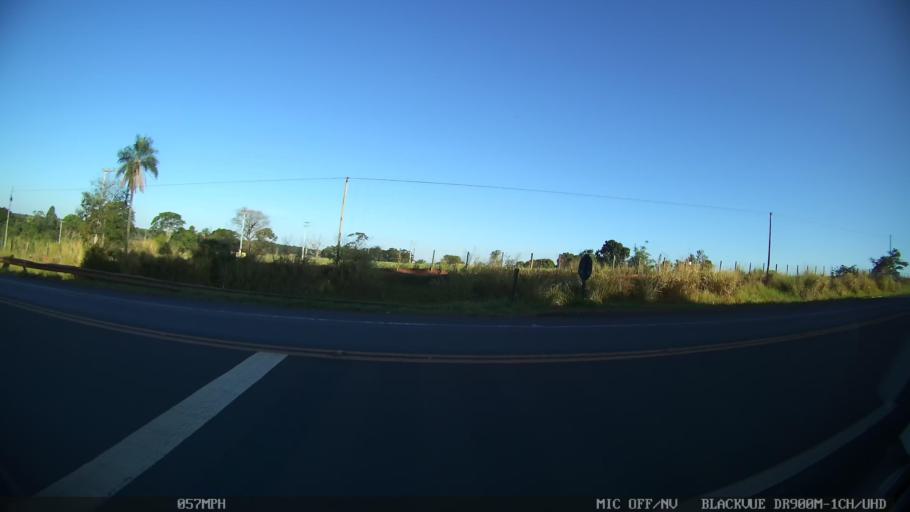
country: BR
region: Sao Paulo
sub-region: Guapiacu
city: Guapiacu
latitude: -20.7633
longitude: -49.1868
